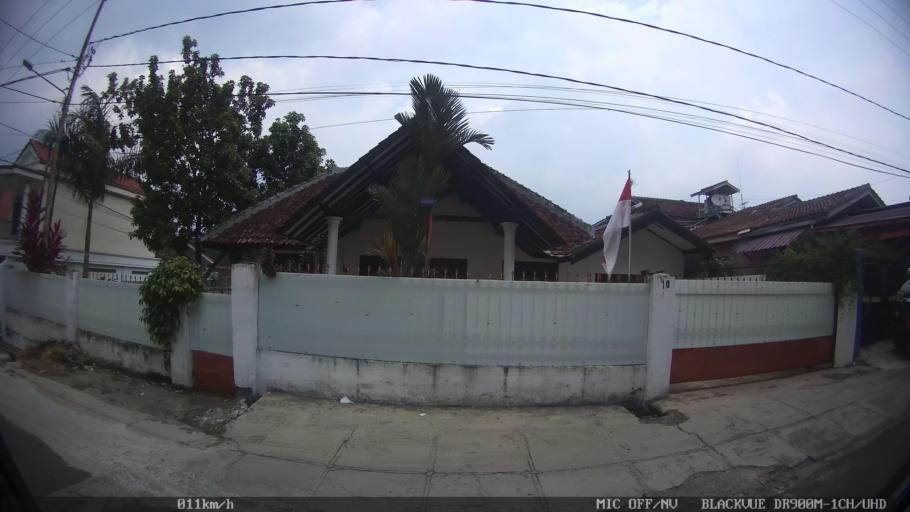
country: ID
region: Lampung
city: Bandarlampung
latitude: -5.4243
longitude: 105.2644
